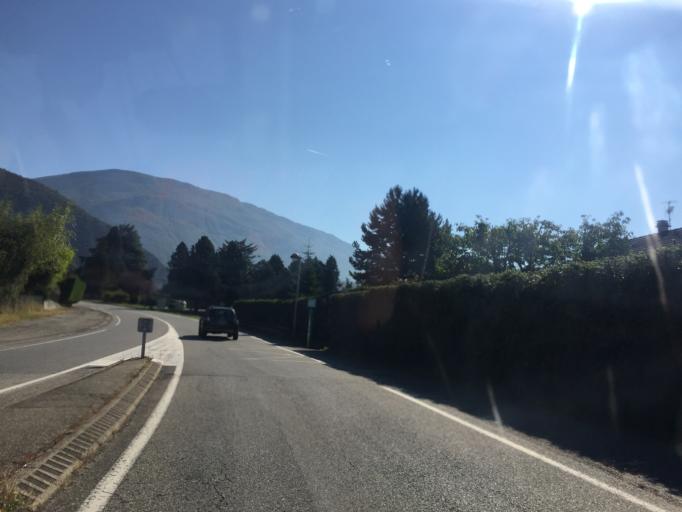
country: FR
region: Rhone-Alpes
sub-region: Departement de la Savoie
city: Challes-les-Eaux
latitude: 45.5438
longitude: 5.9794
